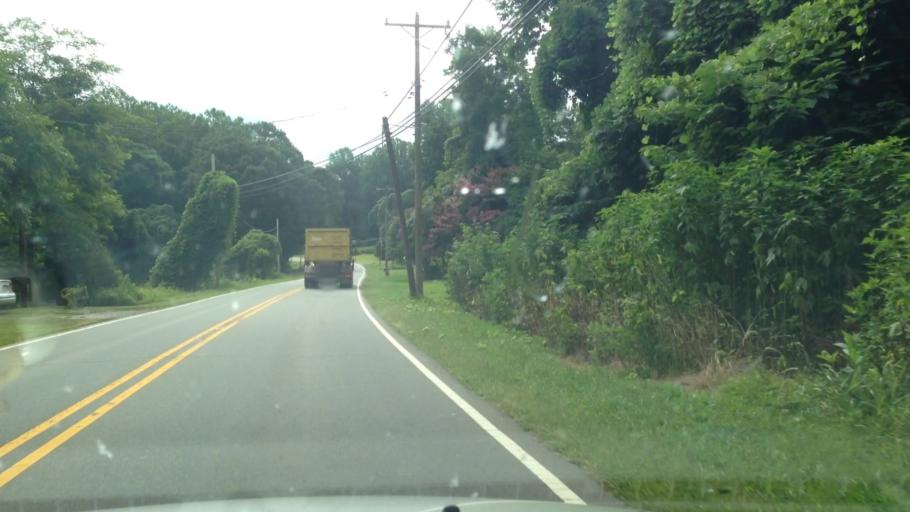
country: US
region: North Carolina
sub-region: Rockingham County
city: Wentworth
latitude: 36.3976
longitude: -79.7674
